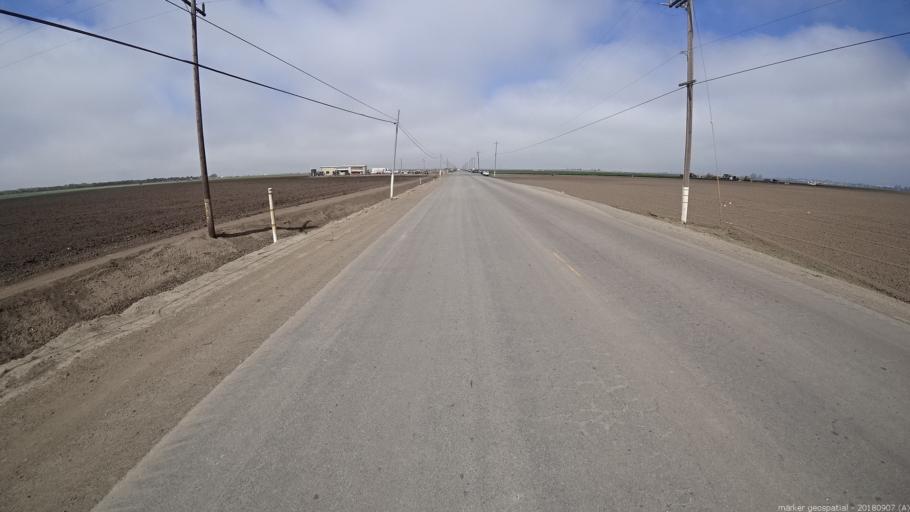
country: US
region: California
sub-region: Monterey County
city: Castroville
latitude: 36.7307
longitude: -121.7541
